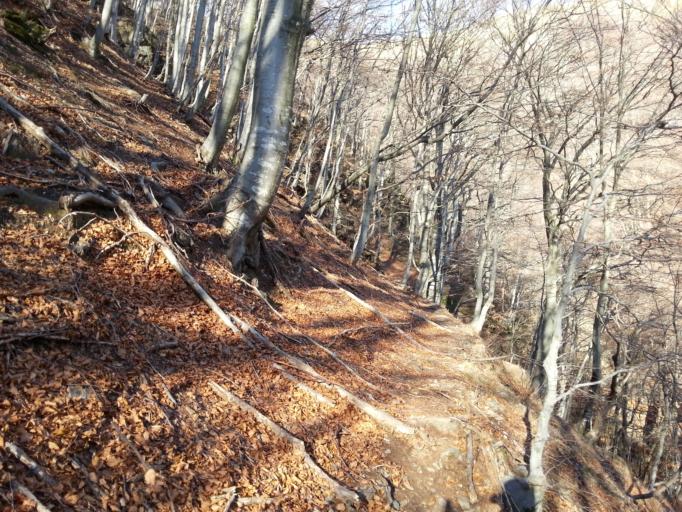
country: CH
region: Ticino
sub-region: Lugano District
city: Gravesano
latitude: 46.0568
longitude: 8.8663
